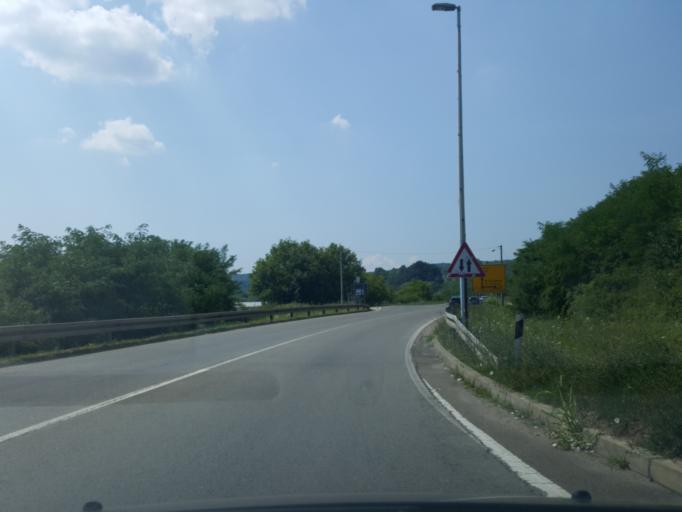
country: RS
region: Central Serbia
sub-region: Belgrade
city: Sopot
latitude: 44.5622
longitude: 20.6694
